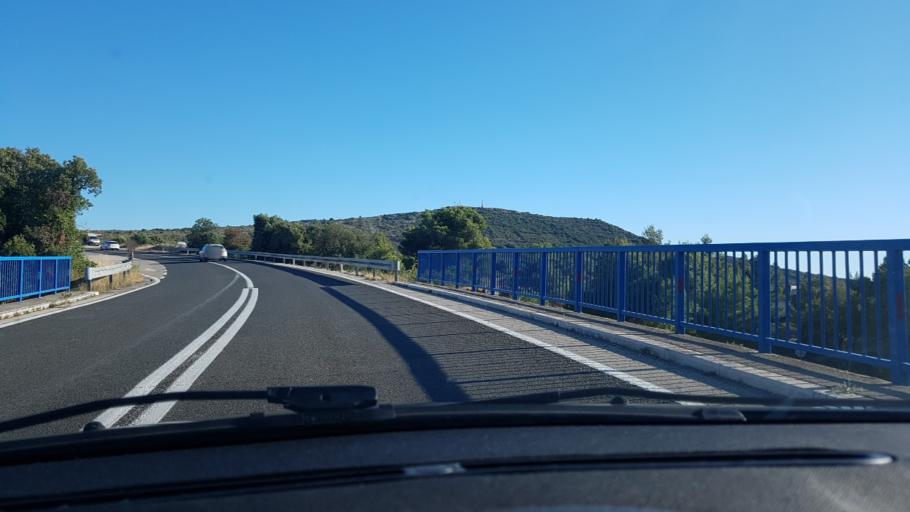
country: HR
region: Sibensko-Kniniska
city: Primosten
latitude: 43.5835
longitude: 15.9345
